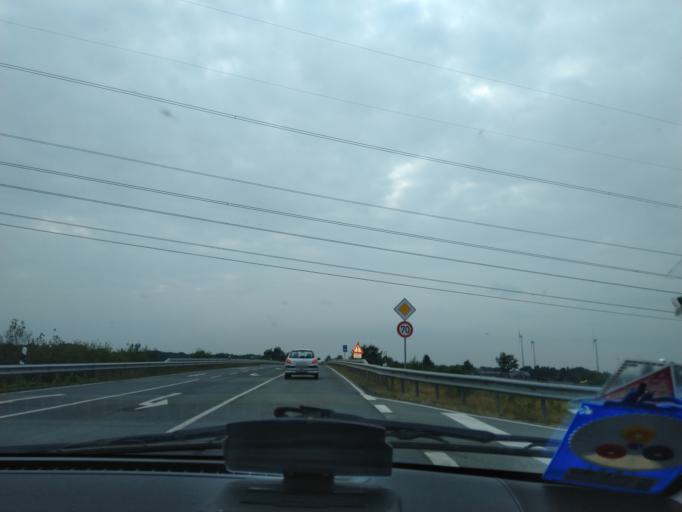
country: DE
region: Lower Saxony
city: Rhede
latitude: 53.0654
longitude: 7.2403
